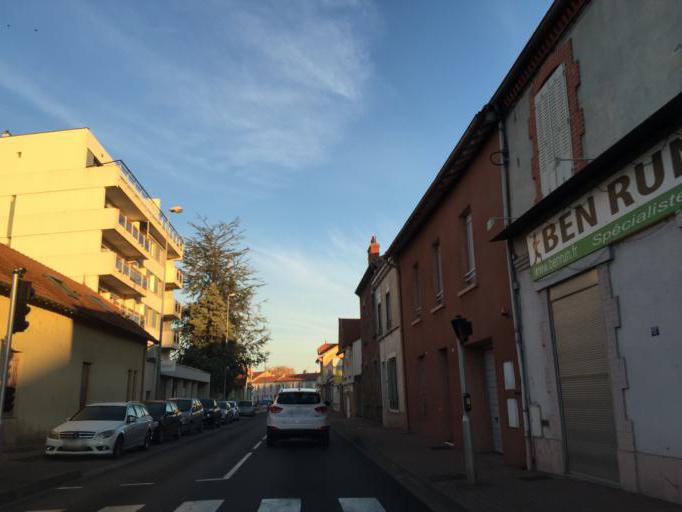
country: FR
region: Rhone-Alpes
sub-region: Departement de la Loire
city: Le Coteau
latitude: 46.0298
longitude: 4.0874
